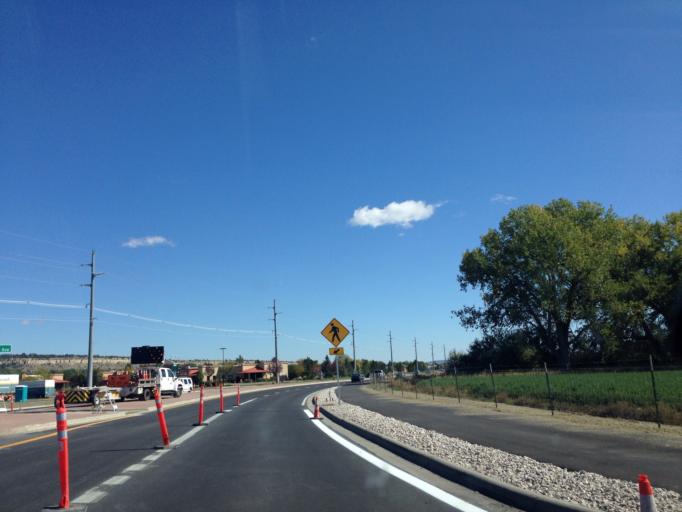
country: US
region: Montana
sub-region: Yellowstone County
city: Billings
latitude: 45.7838
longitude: -108.6112
